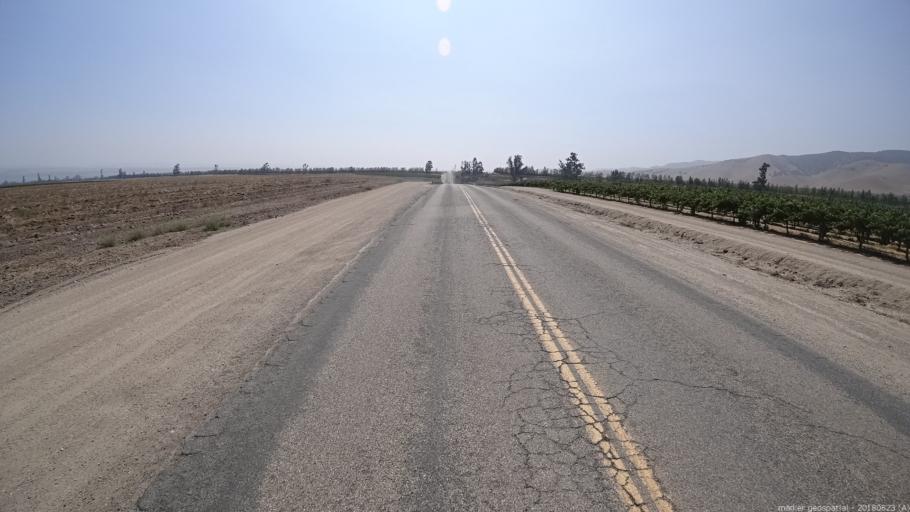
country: US
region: California
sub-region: Monterey County
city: Greenfield
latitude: 36.2610
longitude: -121.2084
